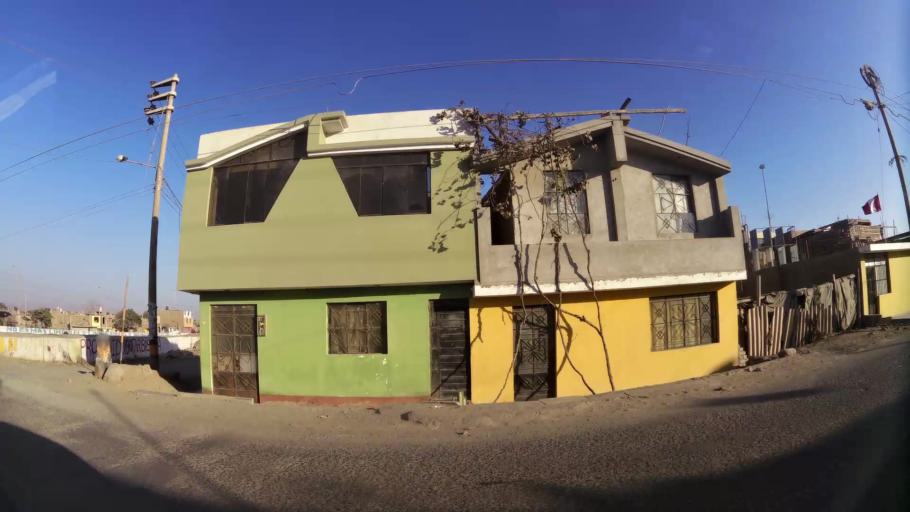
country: PE
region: Ica
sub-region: Provincia de Ica
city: Ica
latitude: -14.0556
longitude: -75.7272
